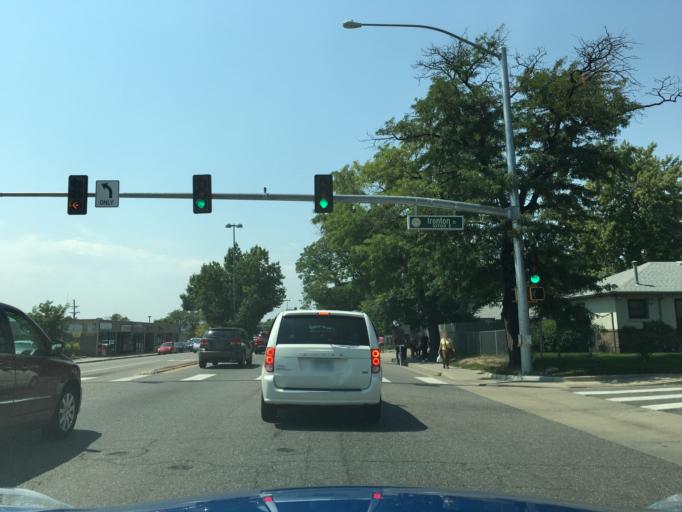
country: US
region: Colorado
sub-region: Adams County
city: Aurora
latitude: 39.7403
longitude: -104.8633
